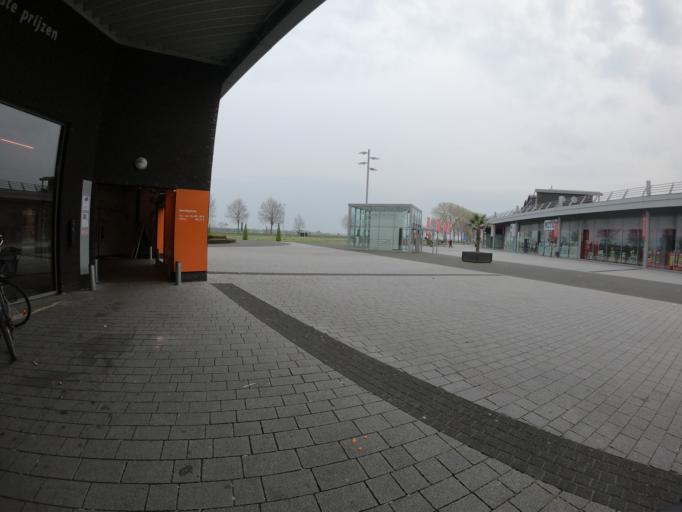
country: BE
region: Flanders
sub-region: Provincie Limburg
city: Maaseik
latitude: 51.0920
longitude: 5.7936
